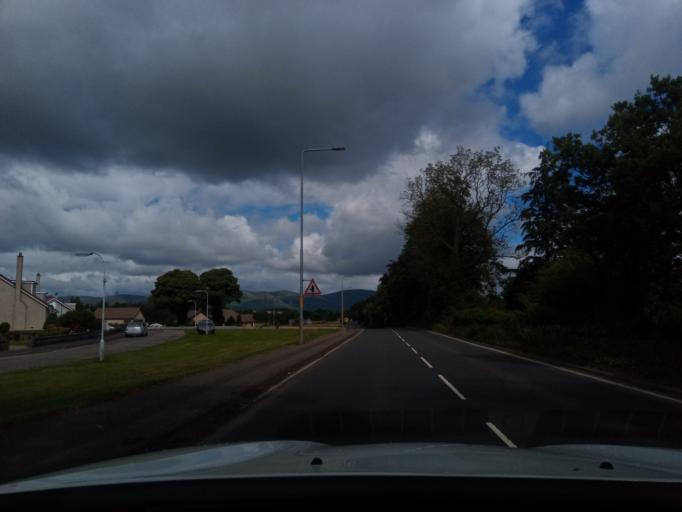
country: GB
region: Scotland
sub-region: Fife
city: Kincardine
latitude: 56.0787
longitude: -3.7203
